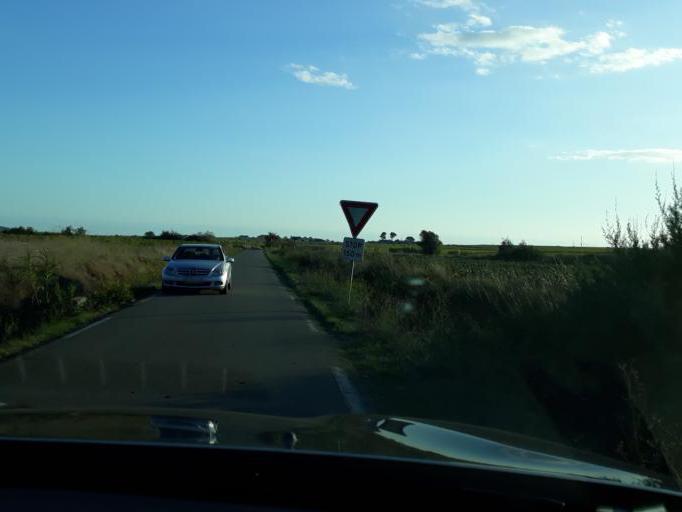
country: FR
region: Languedoc-Roussillon
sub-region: Departement de l'Herault
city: Pomerols
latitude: 43.3629
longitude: 3.4920
